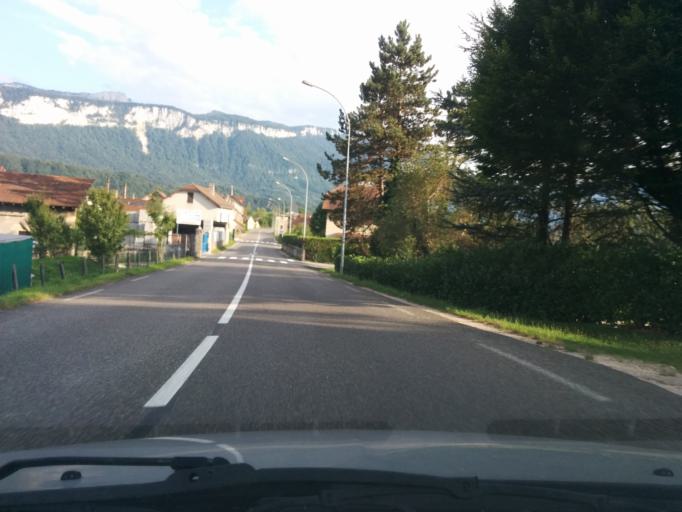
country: FR
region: Rhone-Alpes
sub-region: Departement de la Savoie
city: Les Echelles
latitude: 45.4376
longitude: 5.7511
